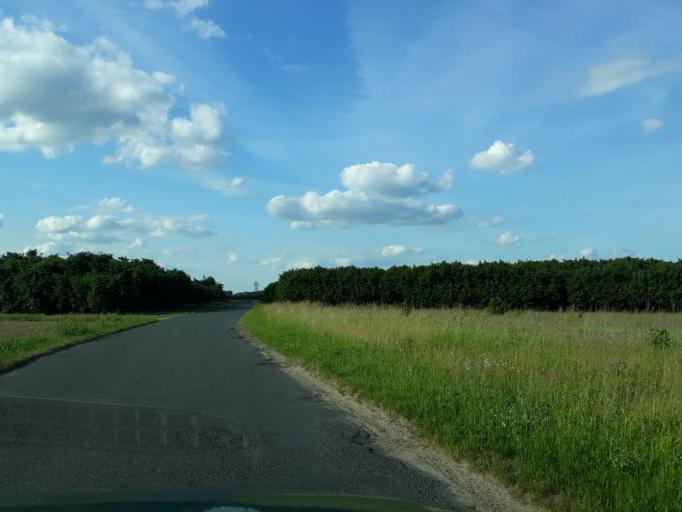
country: FR
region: Centre
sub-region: Departement du Loiret
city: Saint-Hilaire-Saint-Mesmin
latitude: 47.8436
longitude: 1.8224
